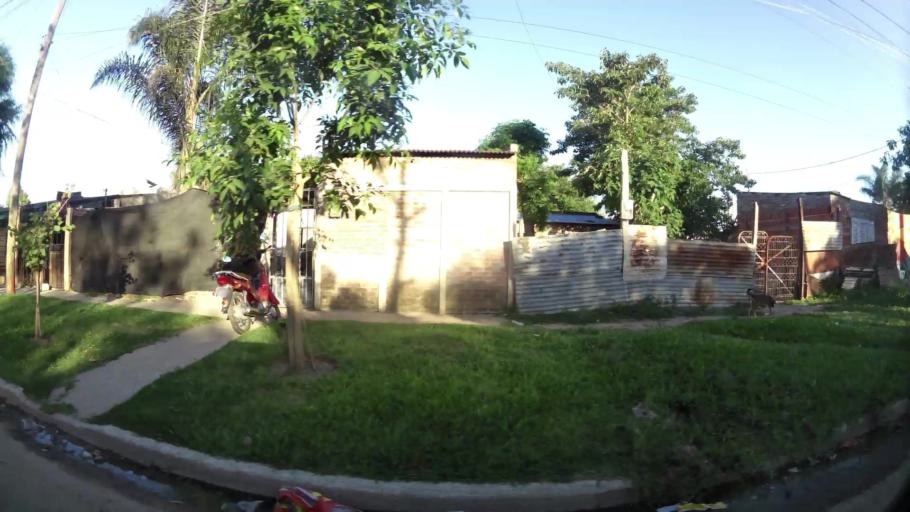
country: AR
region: Santa Fe
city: Santa Fe de la Vera Cruz
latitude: -31.5974
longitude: -60.6771
